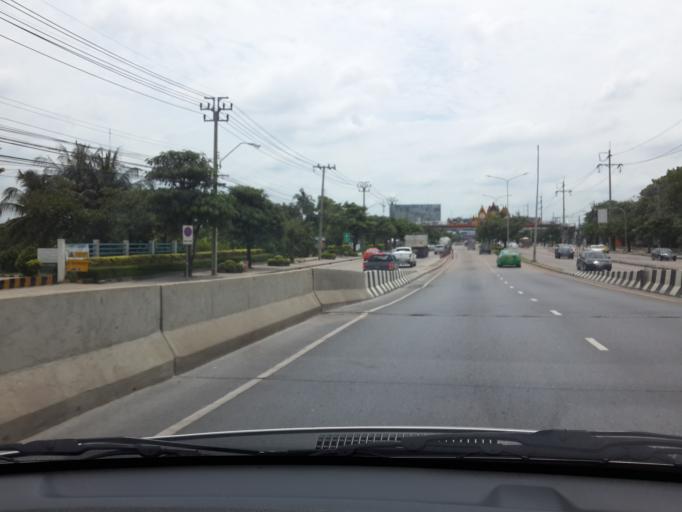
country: TH
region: Bangkok
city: Min Buri
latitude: 13.8139
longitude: 100.7394
